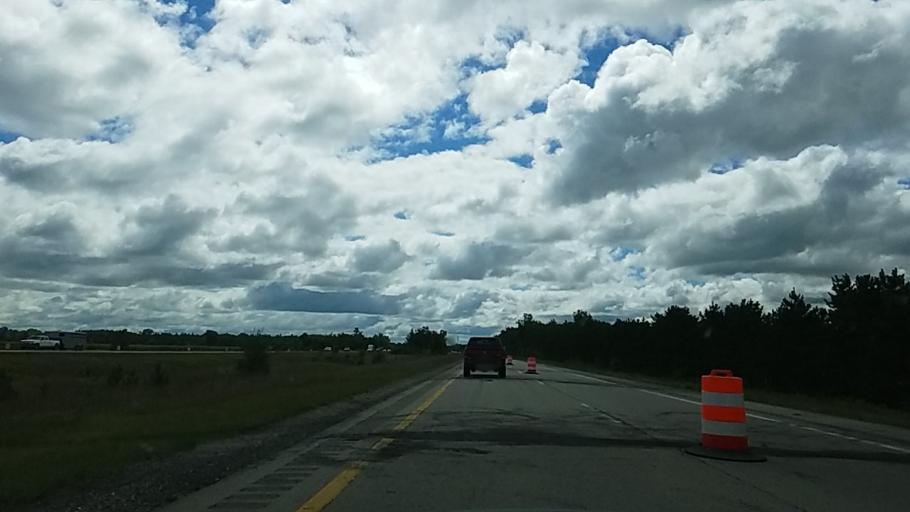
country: US
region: Michigan
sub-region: Arenac County
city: Standish
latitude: 43.9647
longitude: -84.0168
